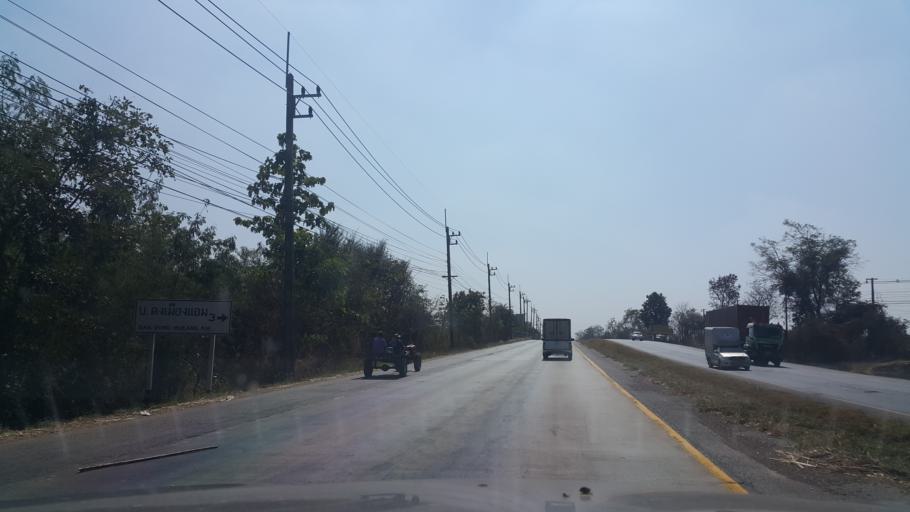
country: TH
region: Khon Kaen
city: Nam Phong
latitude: 16.8145
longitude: 102.8363
